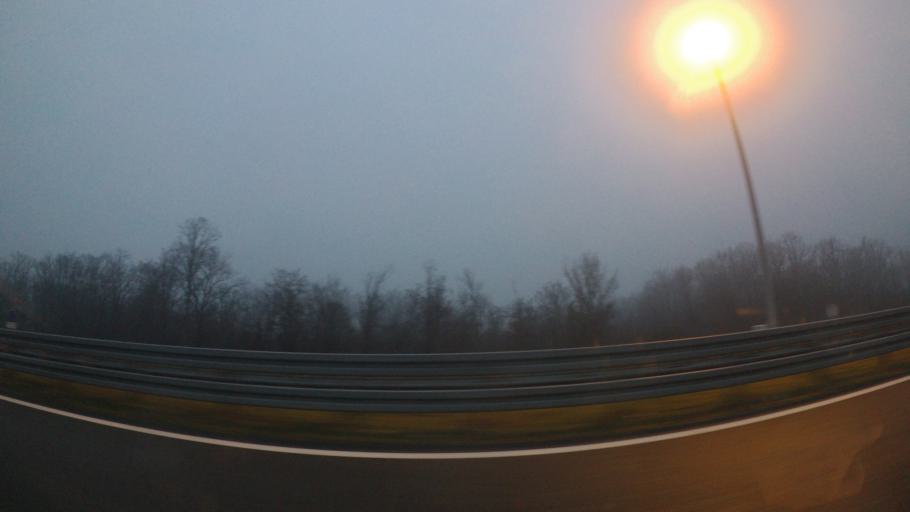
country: HR
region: Zagrebacka
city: Turopolje
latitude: 45.6183
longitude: 16.1066
